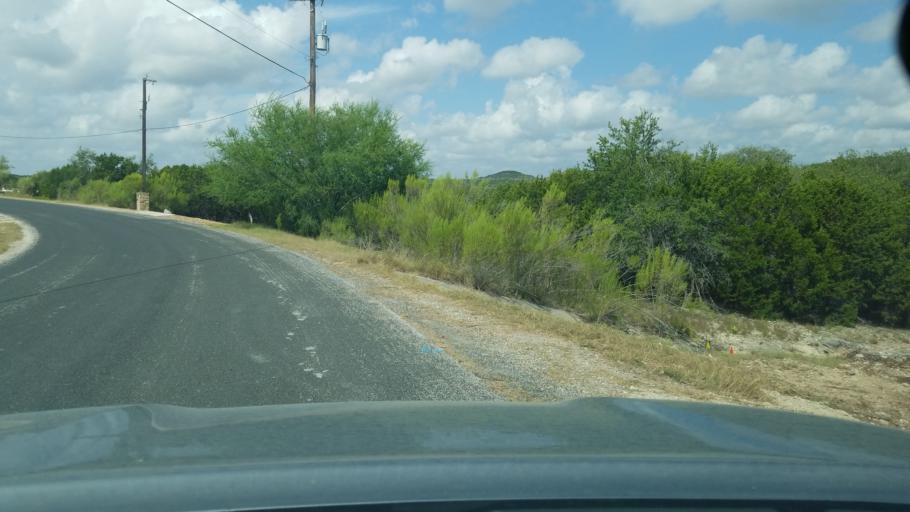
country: US
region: Texas
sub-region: Bexar County
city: Timberwood Park
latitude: 29.6794
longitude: -98.5205
